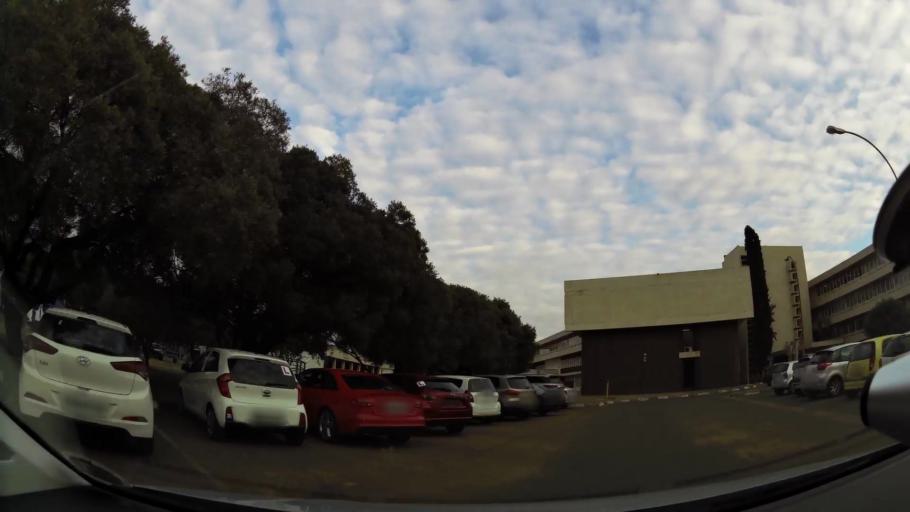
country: ZA
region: Orange Free State
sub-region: Mangaung Metropolitan Municipality
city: Bloemfontein
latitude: -29.1123
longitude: 26.1896
